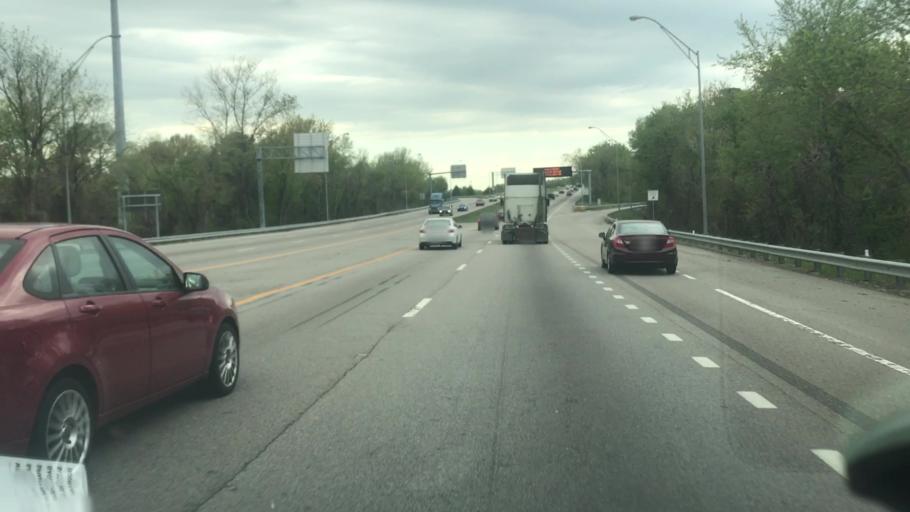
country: US
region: Virginia
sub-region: City of Portsmouth
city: Portsmouth Heights
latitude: 36.8604
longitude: -76.3497
